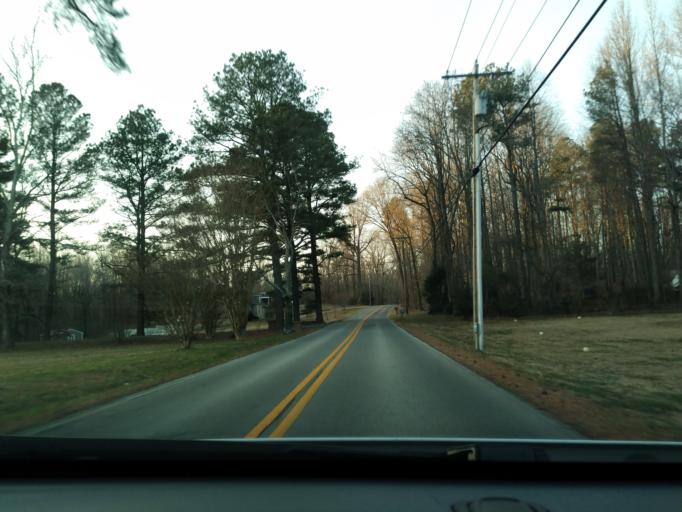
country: US
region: Maryland
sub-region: Calvert County
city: Huntingtown
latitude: 38.6006
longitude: -76.5688
